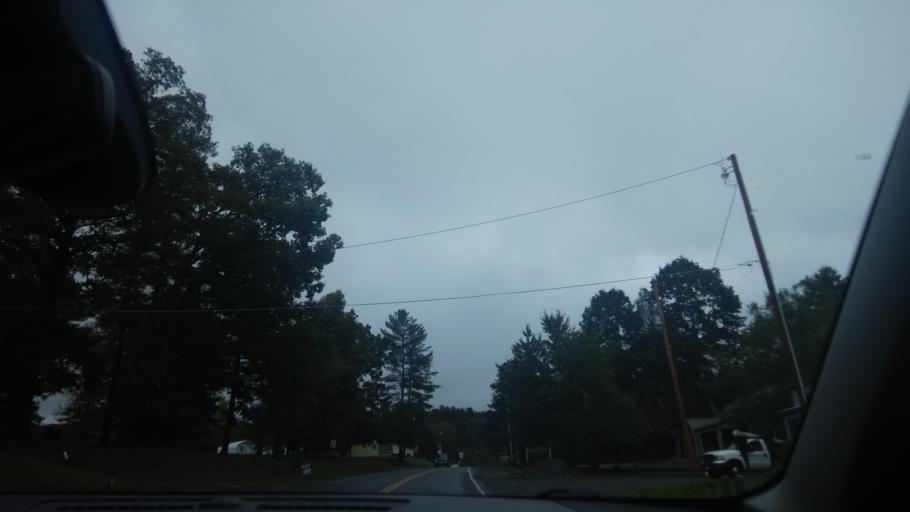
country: US
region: Virginia
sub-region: City of Galax
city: Galax
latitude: 36.6390
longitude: -80.9181
